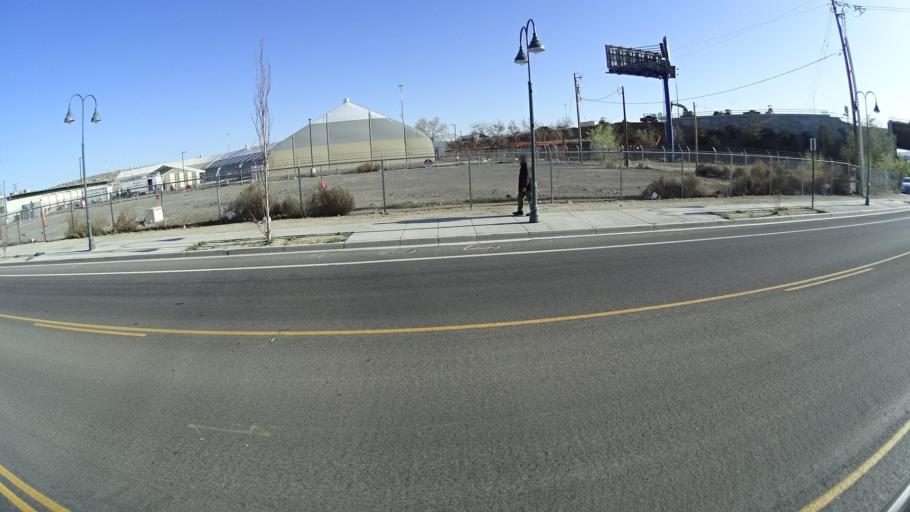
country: US
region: Nevada
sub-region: Washoe County
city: Reno
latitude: 39.5337
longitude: -119.7896
